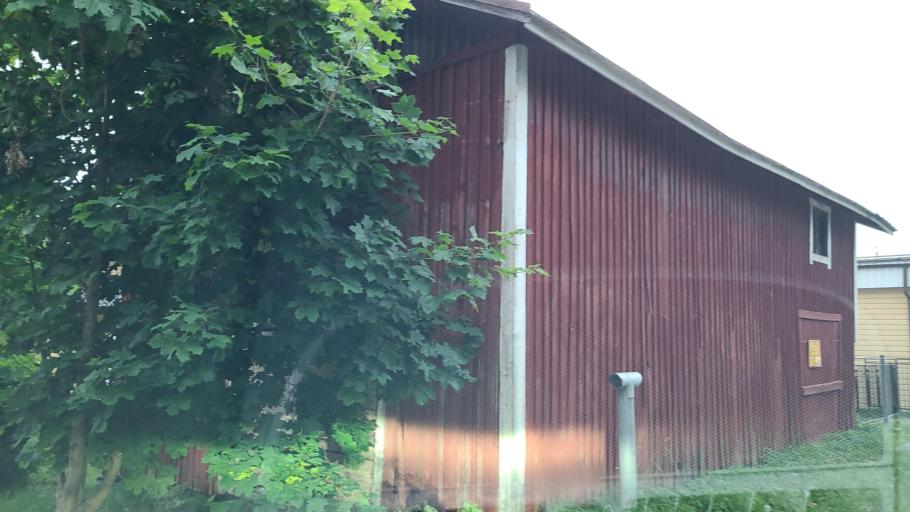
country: FI
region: Ostrobothnia
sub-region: Vaasa
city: Vaasa
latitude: 63.1029
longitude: 21.6177
